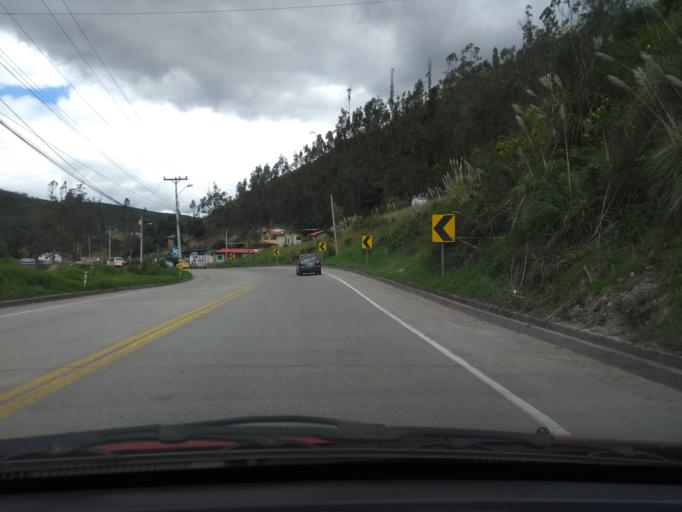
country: EC
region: Azuay
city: Cuenca
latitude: -2.9702
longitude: -79.0481
